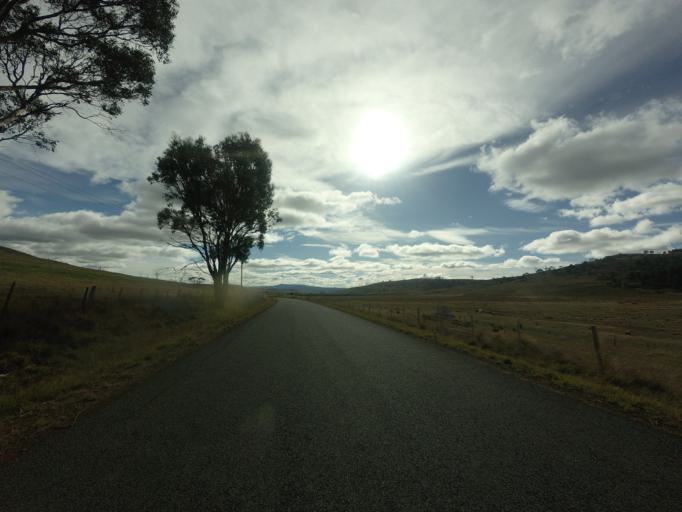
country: AU
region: Tasmania
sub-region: Brighton
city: Bridgewater
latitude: -42.3733
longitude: 147.3568
